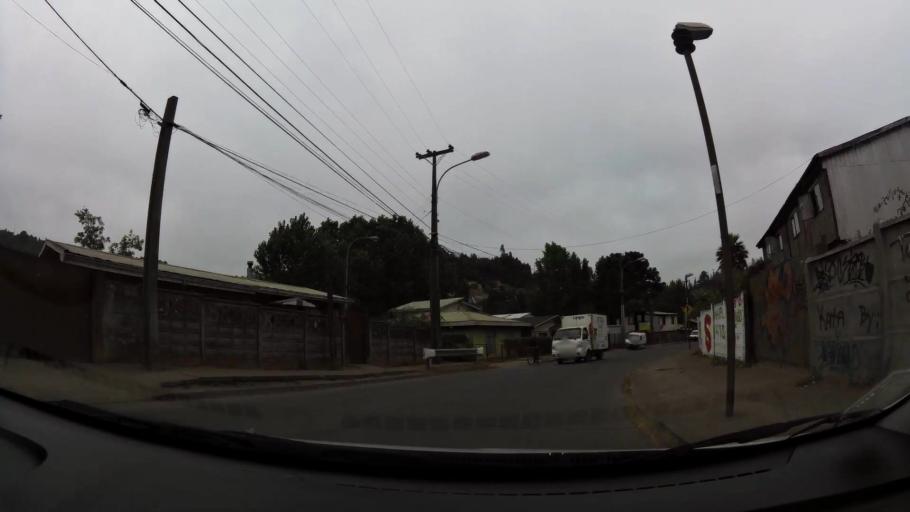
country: CL
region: Biobio
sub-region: Provincia de Concepcion
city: Concepcion
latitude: -36.8355
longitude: -73.0031
